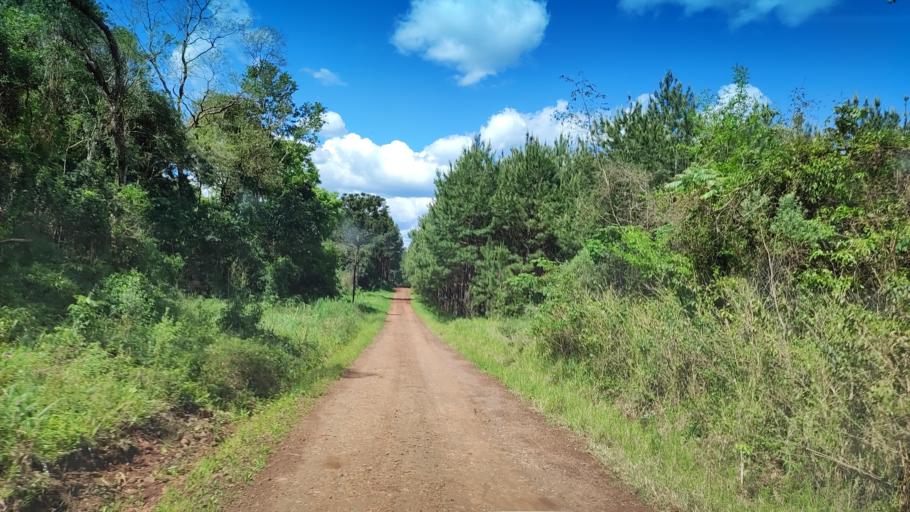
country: AR
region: Misiones
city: Ruiz de Montoya
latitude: -26.9528
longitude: -55.0175
